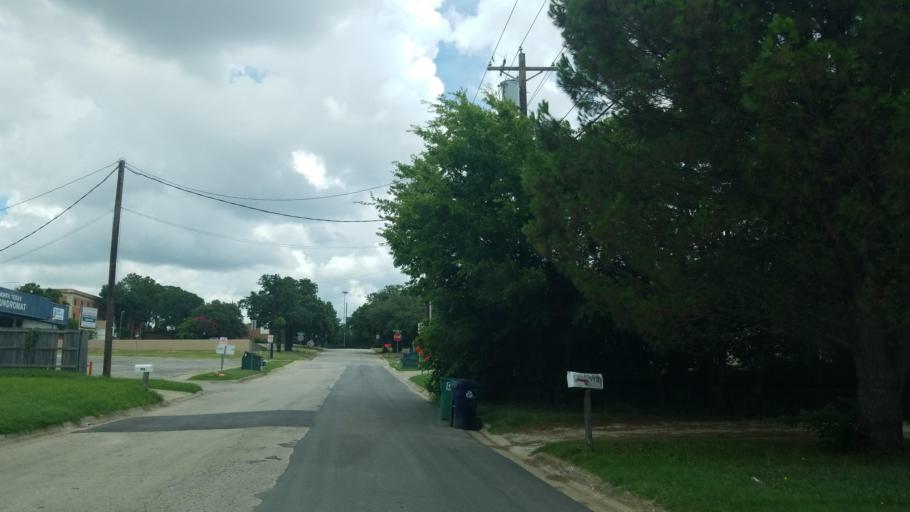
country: US
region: Texas
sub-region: Denton County
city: Denton
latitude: 33.2060
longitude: -97.1486
